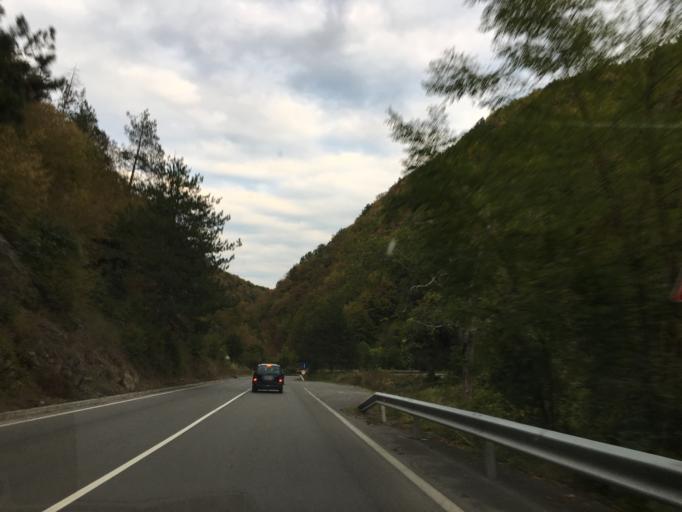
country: BG
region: Sofiya
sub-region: Obshtina Svoge
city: Svoge
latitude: 42.9364
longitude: 23.3885
